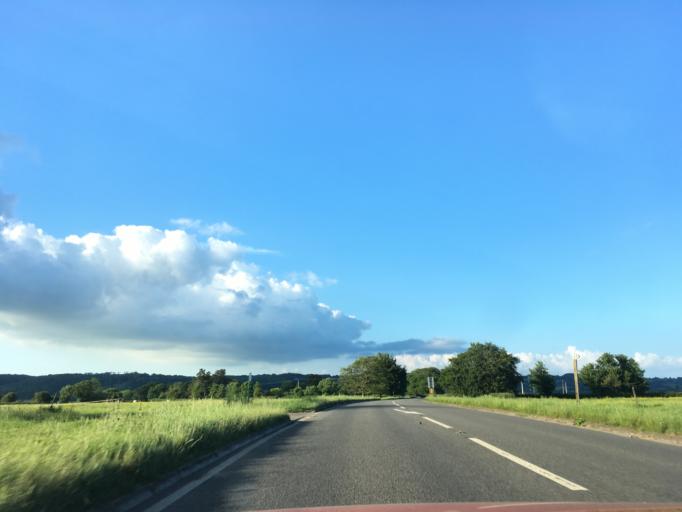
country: GB
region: England
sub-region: North Somerset
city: Burrington
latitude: 51.3430
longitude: -2.7554
